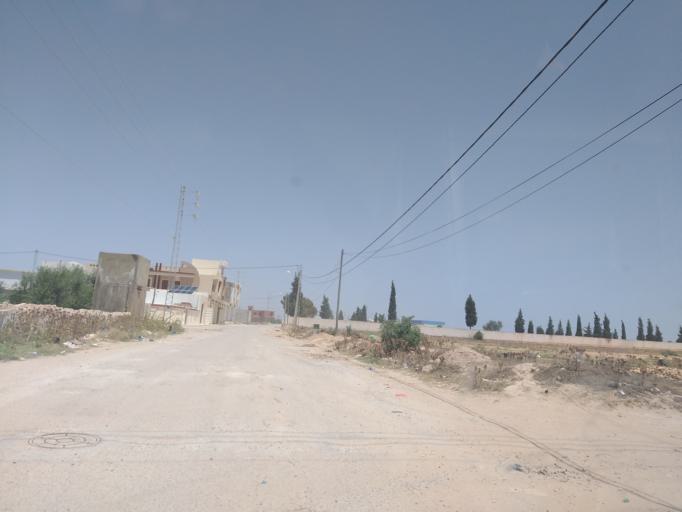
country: TN
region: Al Mahdiyah
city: El Jem
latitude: 35.3089
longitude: 10.7039
